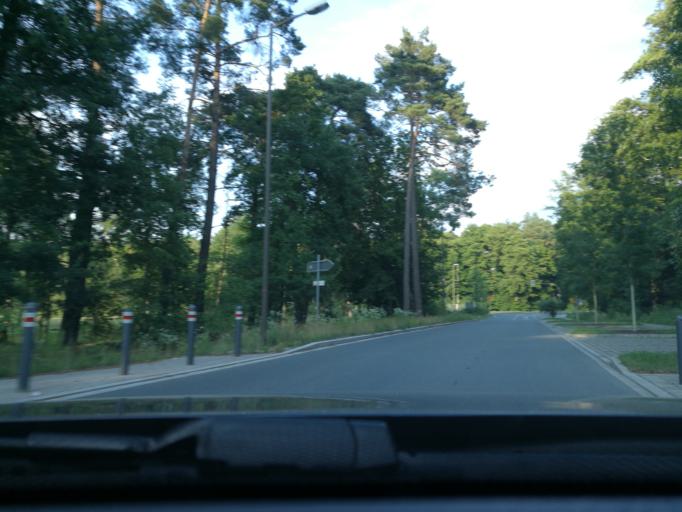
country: DE
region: Bavaria
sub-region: Regierungsbezirk Mittelfranken
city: Buckenhof
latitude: 49.5817
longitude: 11.0316
